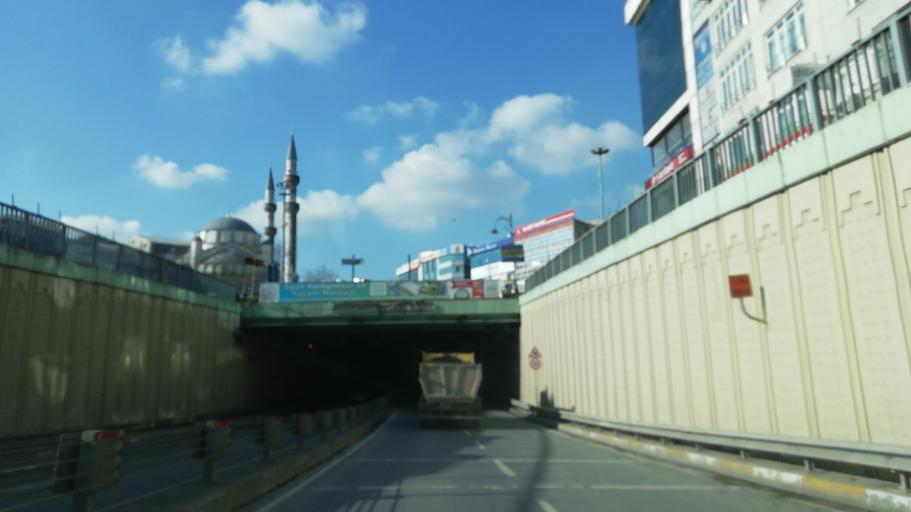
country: TR
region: Istanbul
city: Esenler
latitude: 41.0581
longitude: 28.9146
